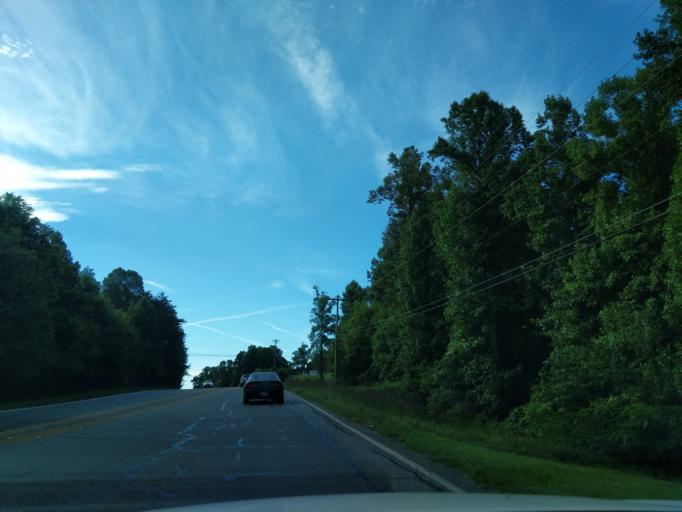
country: US
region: Georgia
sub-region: Fannin County
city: Blue Ridge
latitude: 34.9048
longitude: -84.3748
